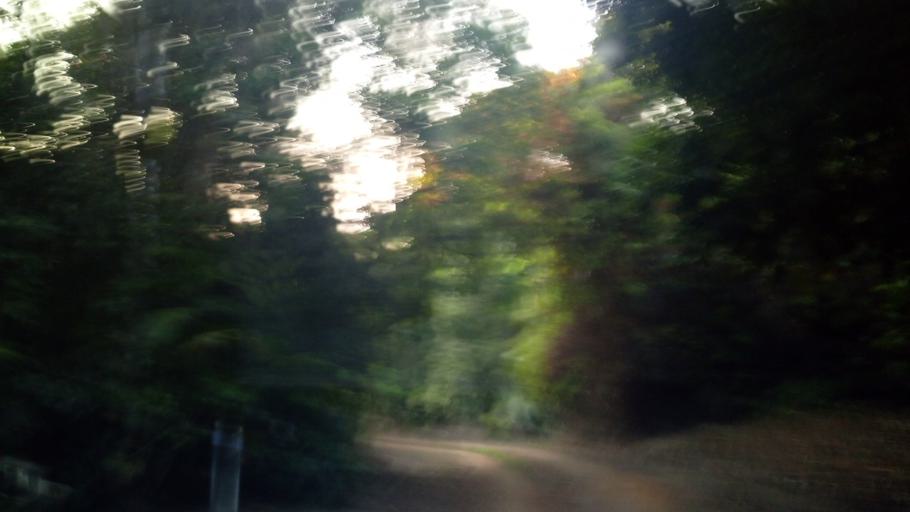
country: AU
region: Queensland
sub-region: Tablelands
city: Atherton
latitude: -17.3753
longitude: 145.7579
